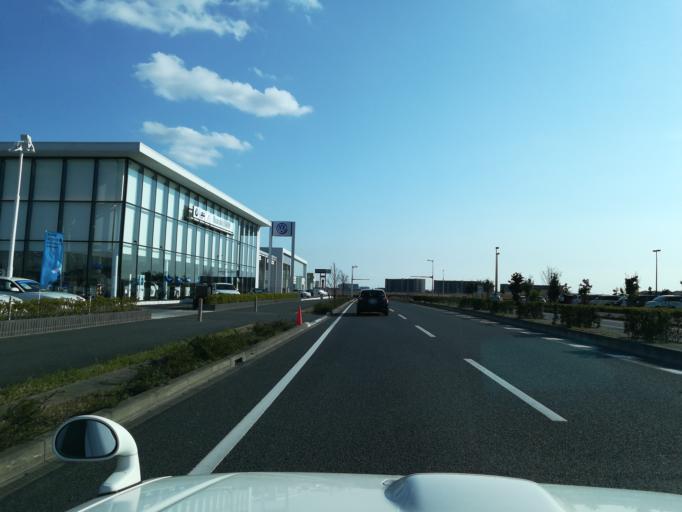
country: JP
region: Ibaraki
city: Naka
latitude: 36.0963
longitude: 140.0814
